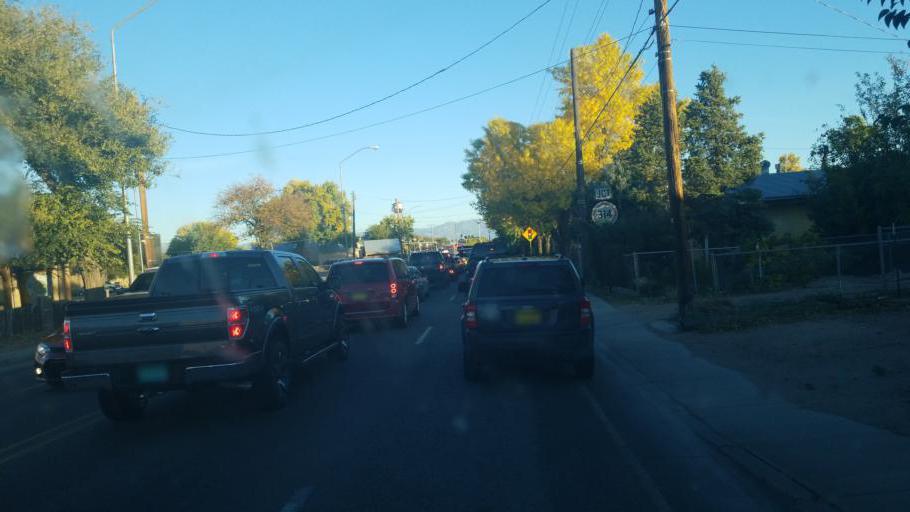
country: US
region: New Mexico
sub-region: Valencia County
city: Los Lunas
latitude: 34.8086
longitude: -106.7380
